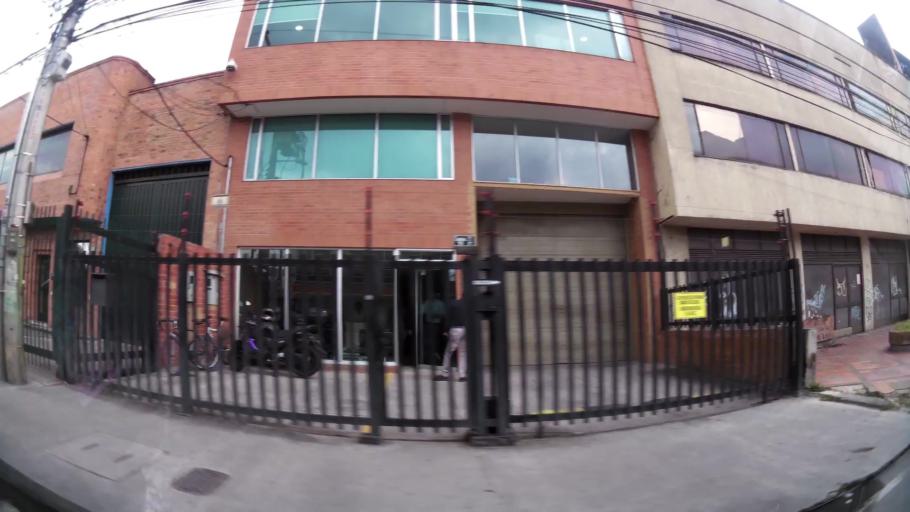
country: CO
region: Cundinamarca
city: La Calera
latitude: 4.7496
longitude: -74.0440
